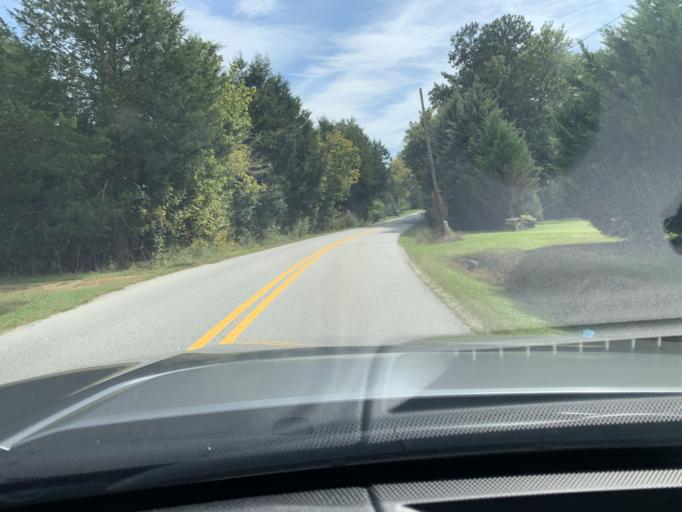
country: US
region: Georgia
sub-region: Polk County
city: Cedartown
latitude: 33.9738
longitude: -85.2728
